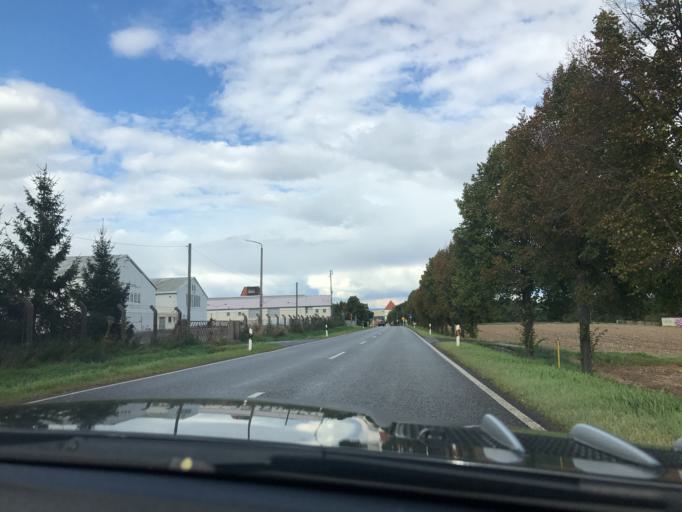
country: DE
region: Thuringia
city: Bad Langensalza
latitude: 51.0973
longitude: 10.6444
